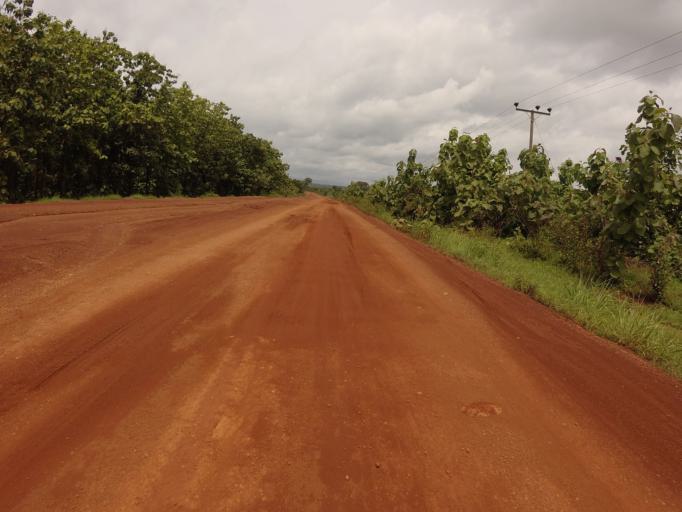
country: GH
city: Kpandae
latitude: 8.4088
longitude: 0.3956
